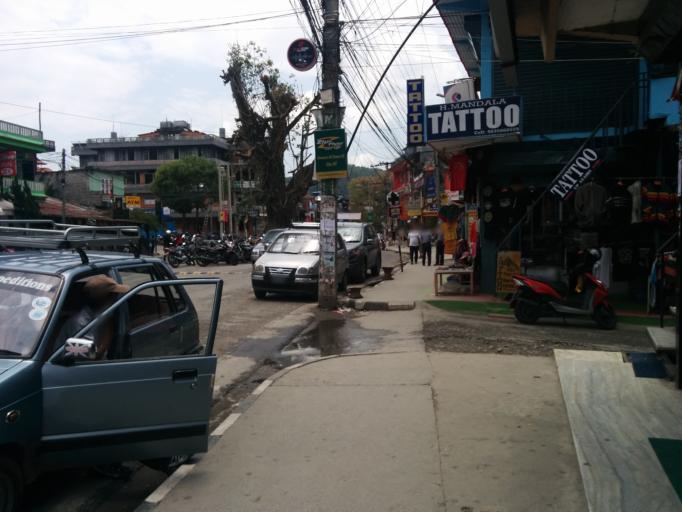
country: NP
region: Western Region
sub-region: Gandaki Zone
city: Pokhara
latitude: 28.2123
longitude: 83.9570
